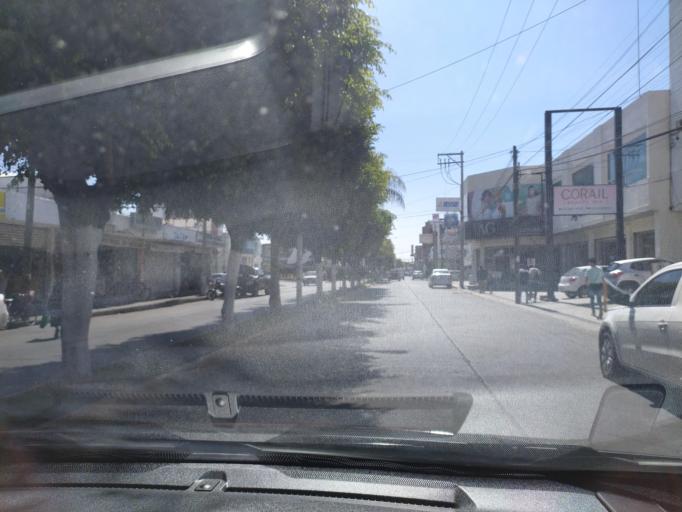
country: LA
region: Oudomxai
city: Muang La
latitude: 21.0161
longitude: 101.8612
